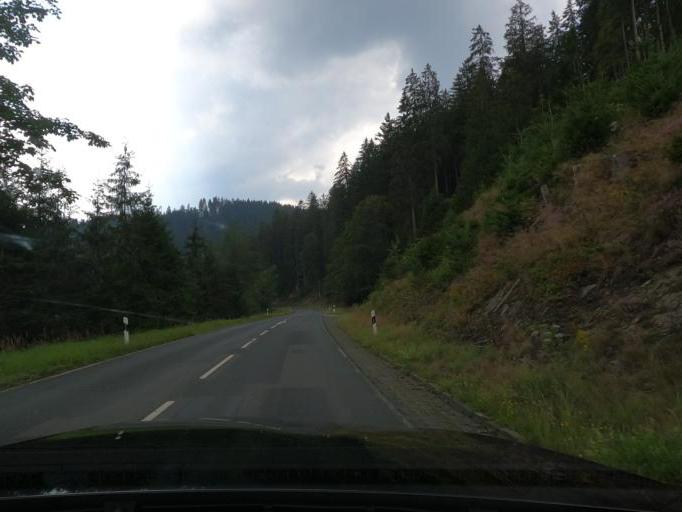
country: DE
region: Lower Saxony
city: Wildemann
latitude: 51.8329
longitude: 10.2734
